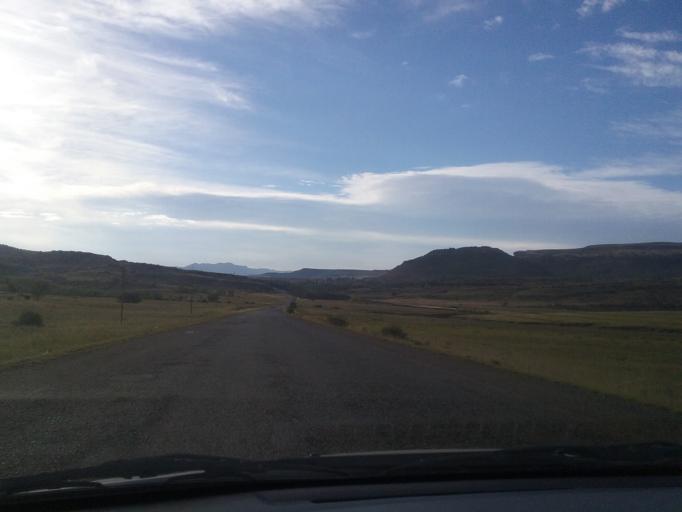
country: LS
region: Quthing
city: Quthing
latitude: -30.3844
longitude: 27.5947
